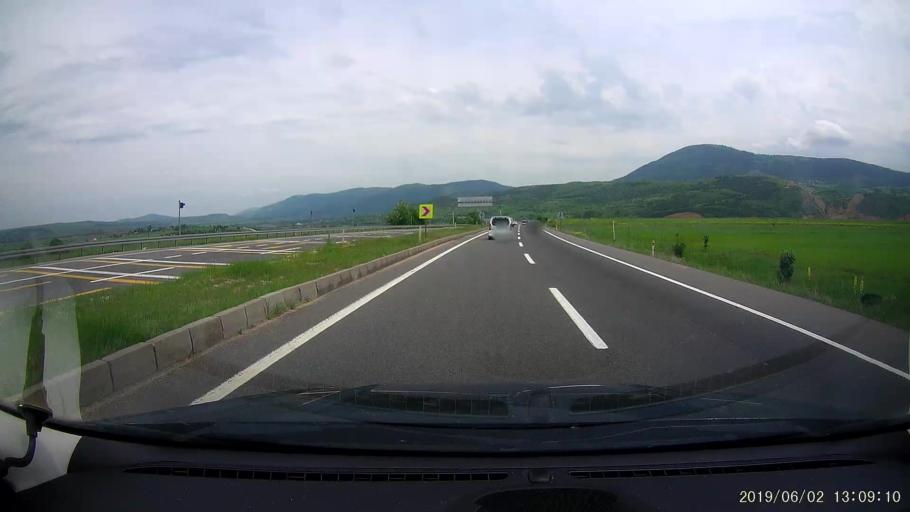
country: TR
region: Karabuk
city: Gozyeri
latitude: 40.8708
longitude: 32.5826
